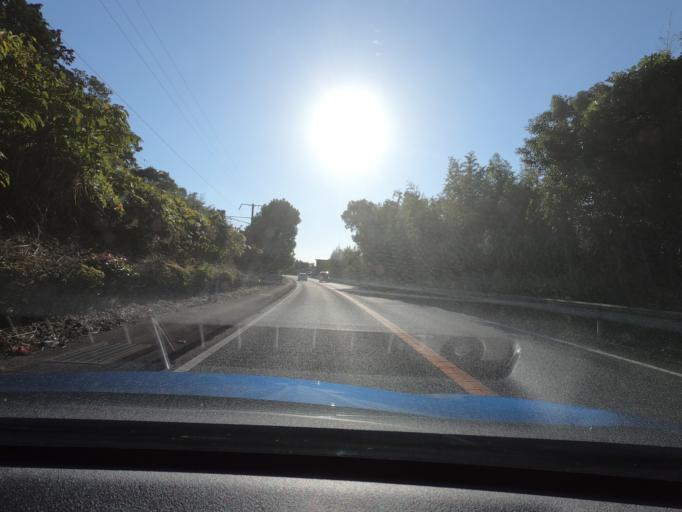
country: JP
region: Kagoshima
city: Izumi
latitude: 32.1459
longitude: 130.3575
